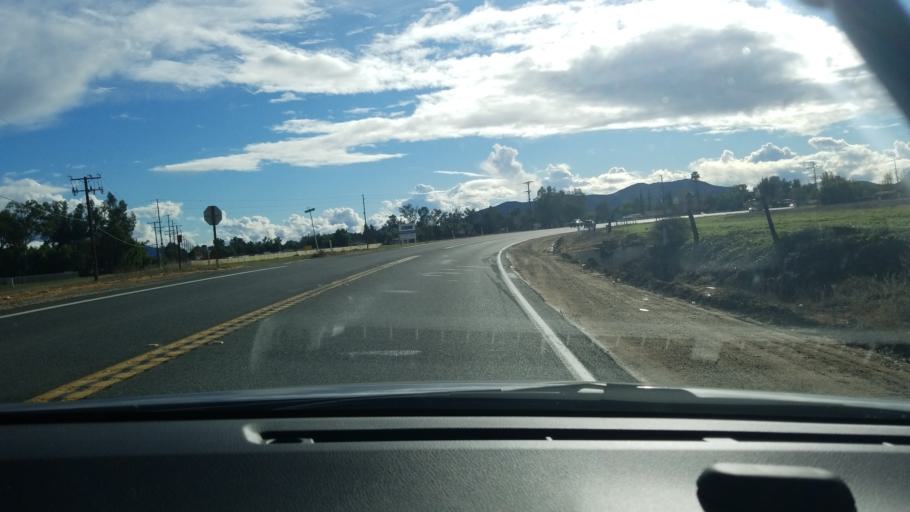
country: US
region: California
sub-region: Riverside County
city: Winchester
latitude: 33.7167
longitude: -117.0766
